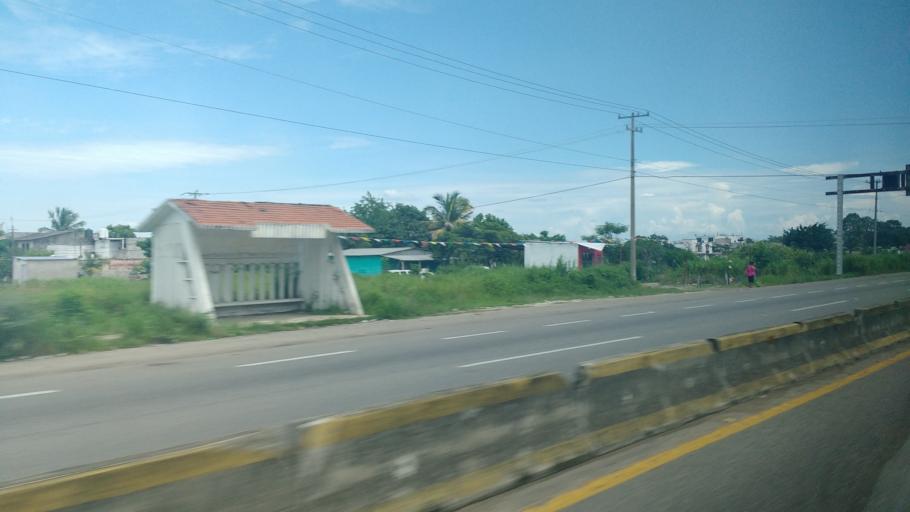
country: MX
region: Tabasco
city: Parrilla
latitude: 17.9048
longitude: -92.9226
